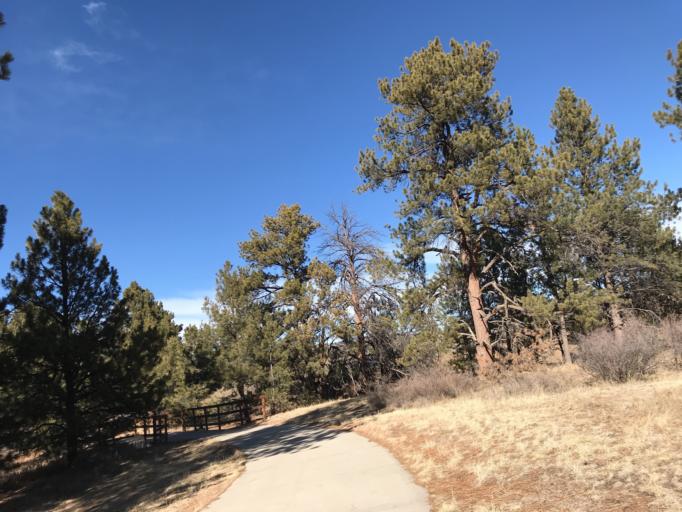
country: US
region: Colorado
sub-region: Douglas County
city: Castle Pines
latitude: 39.4103
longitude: -104.8898
